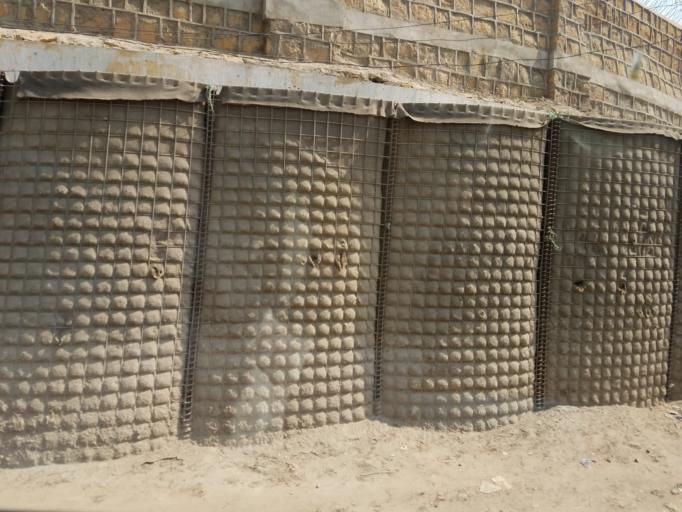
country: PK
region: Sindh
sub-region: Karachi District
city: Karachi
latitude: 24.8887
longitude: 67.0512
